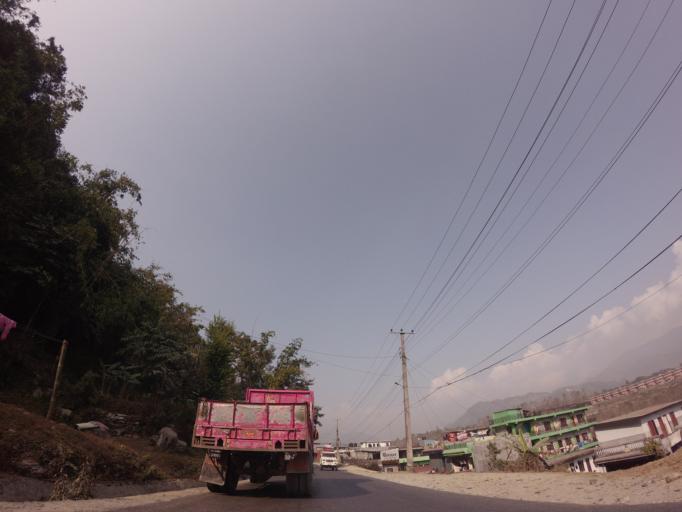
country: NP
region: Western Region
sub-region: Gandaki Zone
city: Pokhara
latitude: 28.2476
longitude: 83.9767
